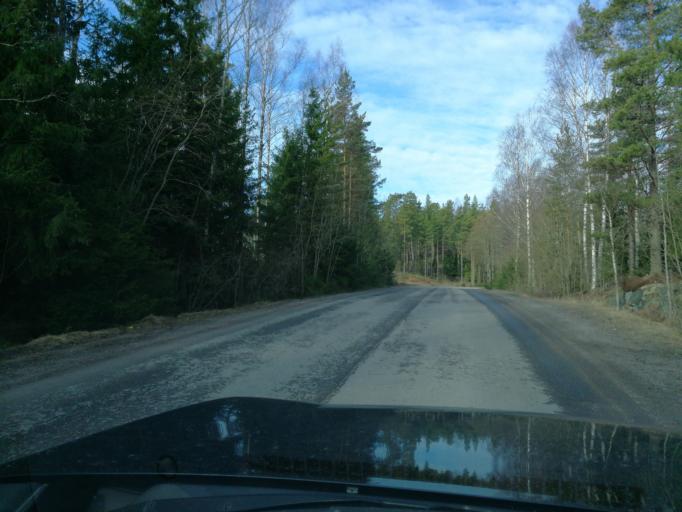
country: FI
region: Uusimaa
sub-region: Helsinki
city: Kirkkonummi
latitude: 60.0911
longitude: 24.3710
